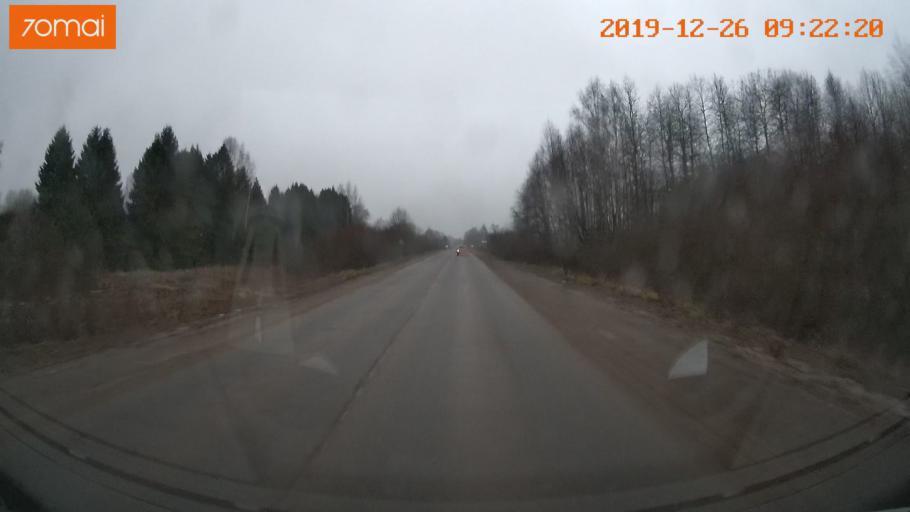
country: RU
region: Vologda
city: Gryazovets
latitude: 58.9793
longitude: 40.2168
